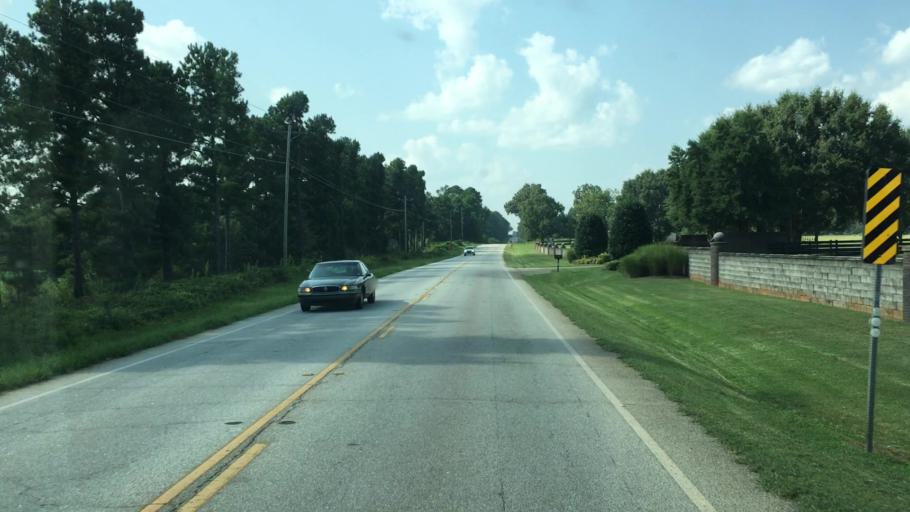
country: US
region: Georgia
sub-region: Walton County
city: Social Circle
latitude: 33.5677
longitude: -83.7389
